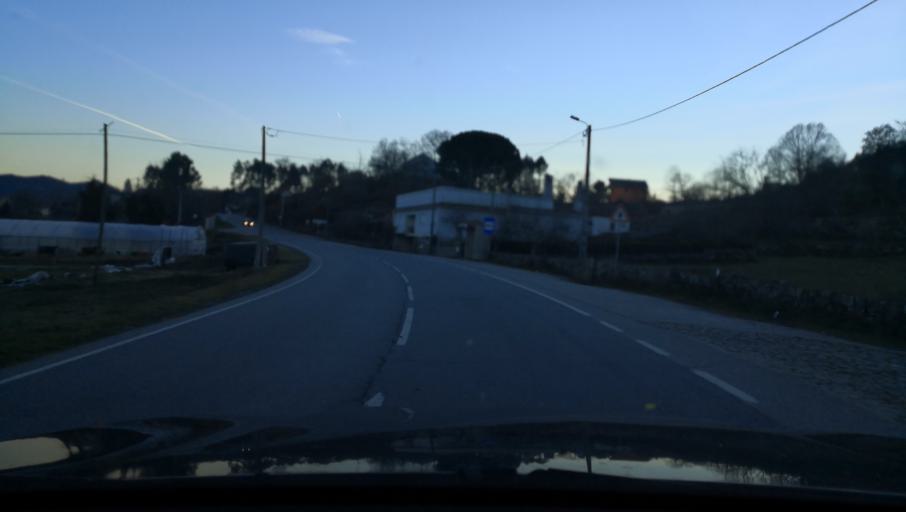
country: PT
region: Vila Real
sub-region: Vila Pouca de Aguiar
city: Vila Pouca de Aguiar
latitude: 41.4254
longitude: -7.6849
